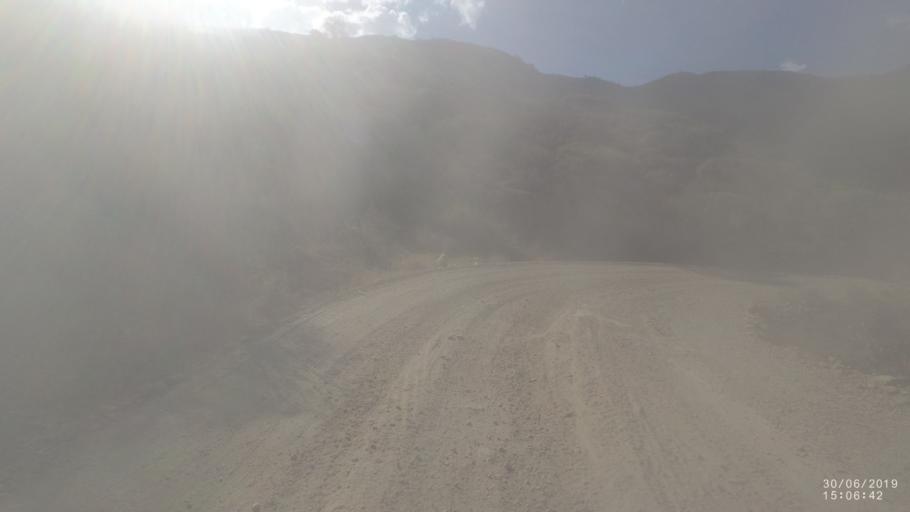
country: BO
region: Cochabamba
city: Irpa Irpa
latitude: -17.7310
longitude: -66.3097
